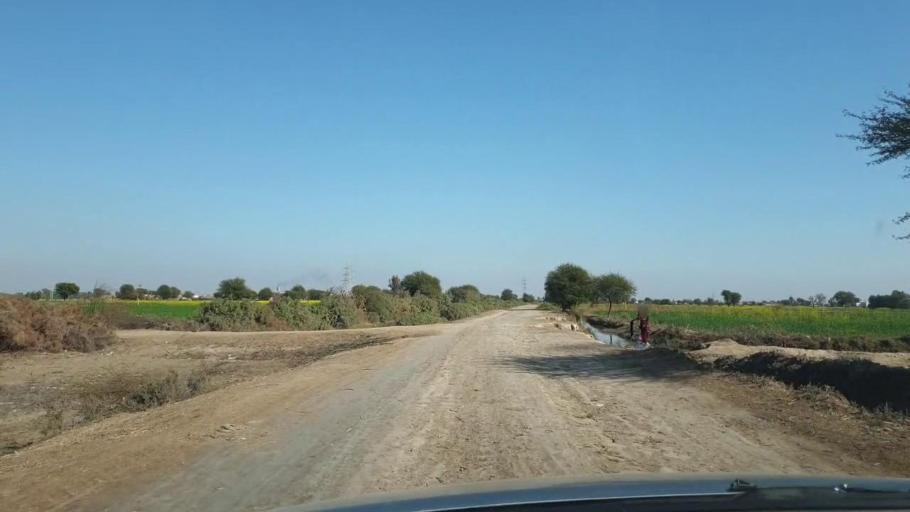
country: PK
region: Sindh
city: Jhol
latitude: 25.9259
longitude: 68.9923
